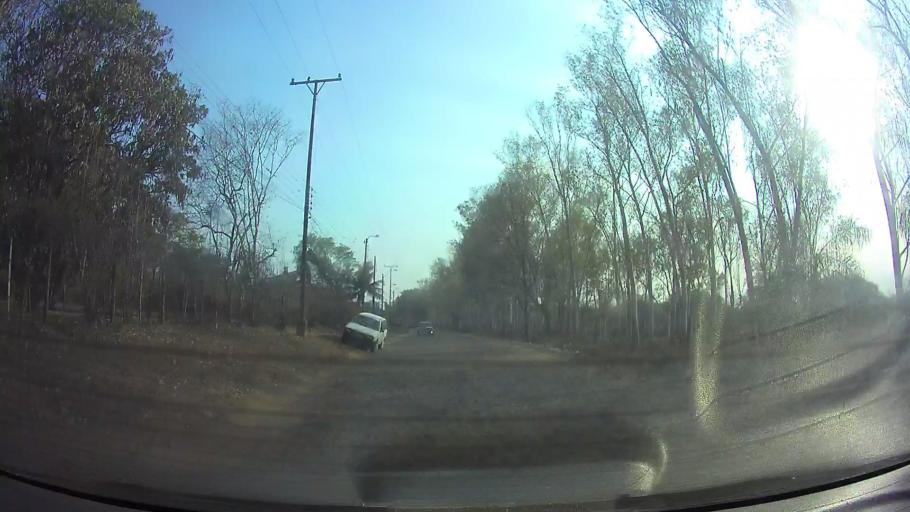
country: PY
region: Central
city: Limpio
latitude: -25.2219
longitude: -57.5050
